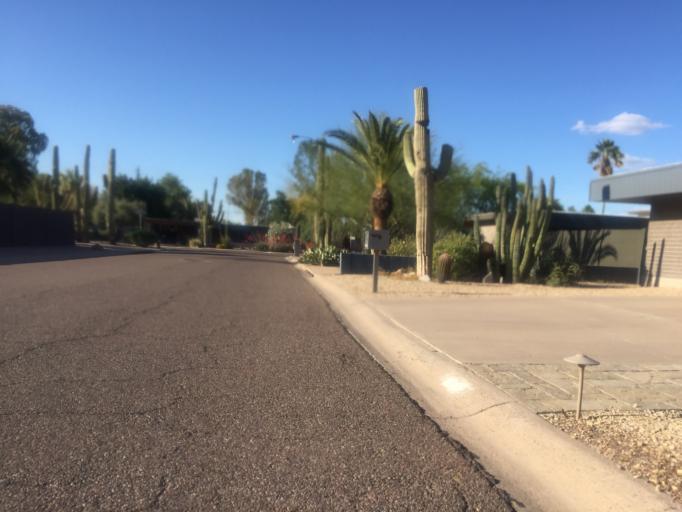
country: US
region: Arizona
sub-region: Maricopa County
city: Paradise Valley
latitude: 33.5781
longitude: -112.0056
